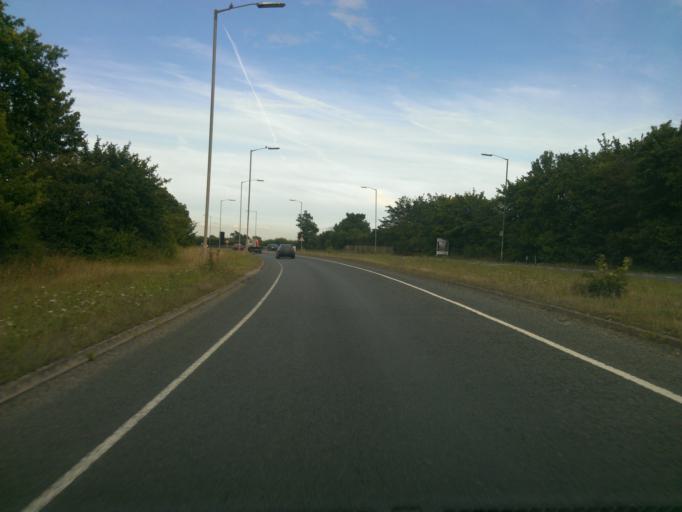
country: GB
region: England
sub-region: Essex
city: Coggeshall
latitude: 51.8729
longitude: 0.7046
